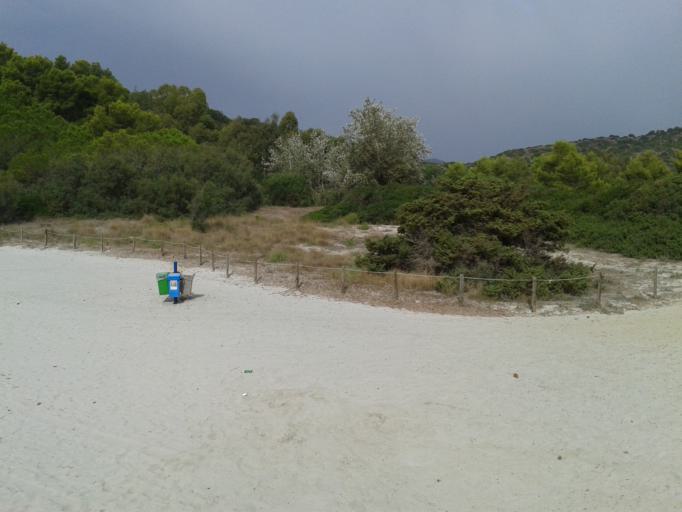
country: IT
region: Sardinia
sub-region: Provincia di Cagliari
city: Villasimius
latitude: 39.1303
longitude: 9.5351
